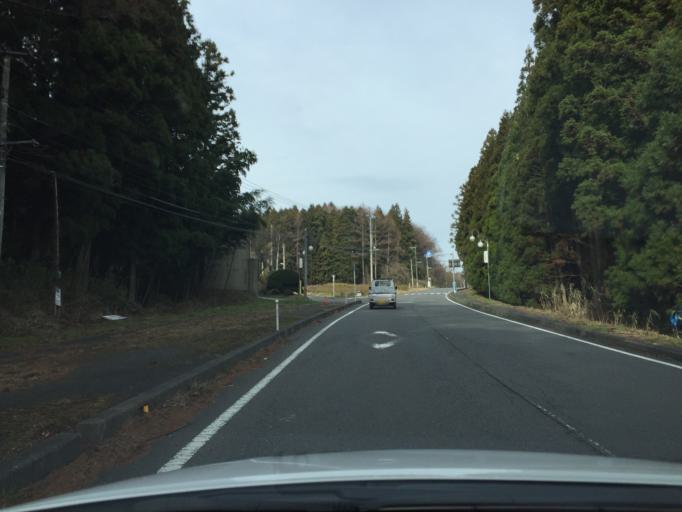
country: JP
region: Fukushima
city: Funehikimachi-funehiki
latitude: 37.3845
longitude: 140.5909
